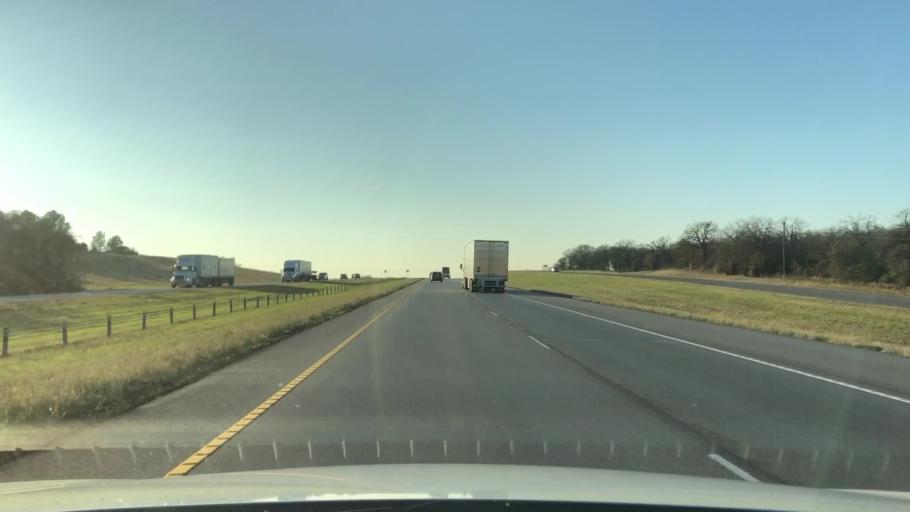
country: US
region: Texas
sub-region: Caldwell County
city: Luling
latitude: 29.6533
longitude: -97.5524
